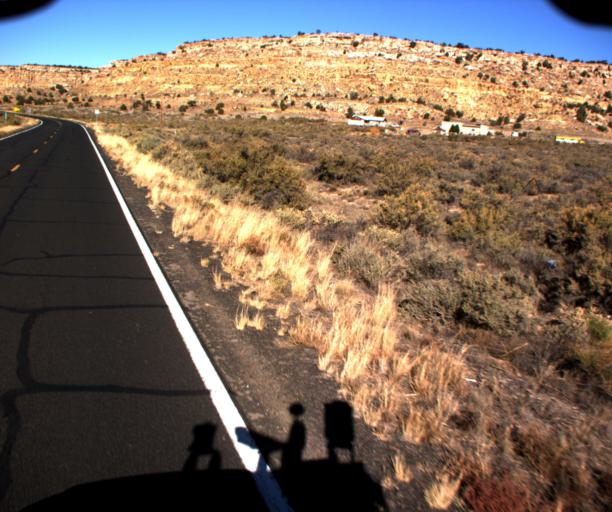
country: US
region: Arizona
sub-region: Navajo County
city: First Mesa
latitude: 35.8416
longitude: -110.2419
